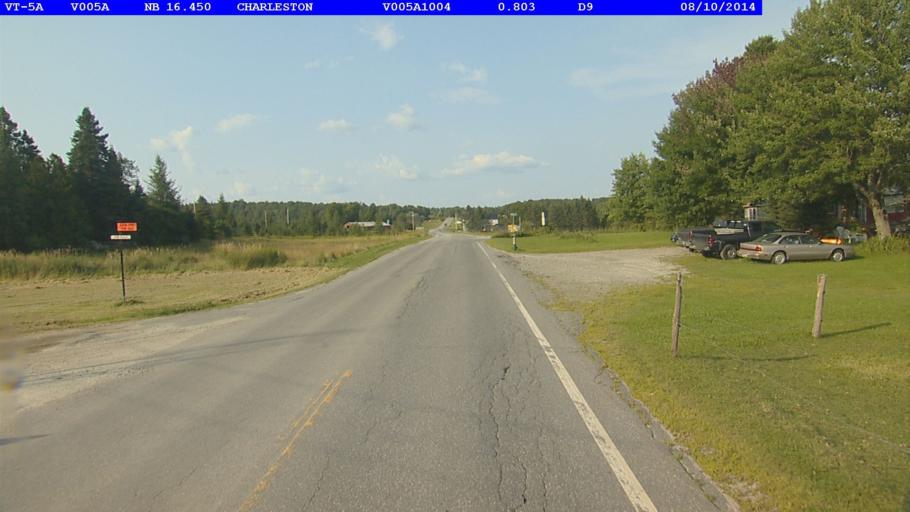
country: US
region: Vermont
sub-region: Orleans County
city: Newport
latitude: 44.8452
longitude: -72.0587
